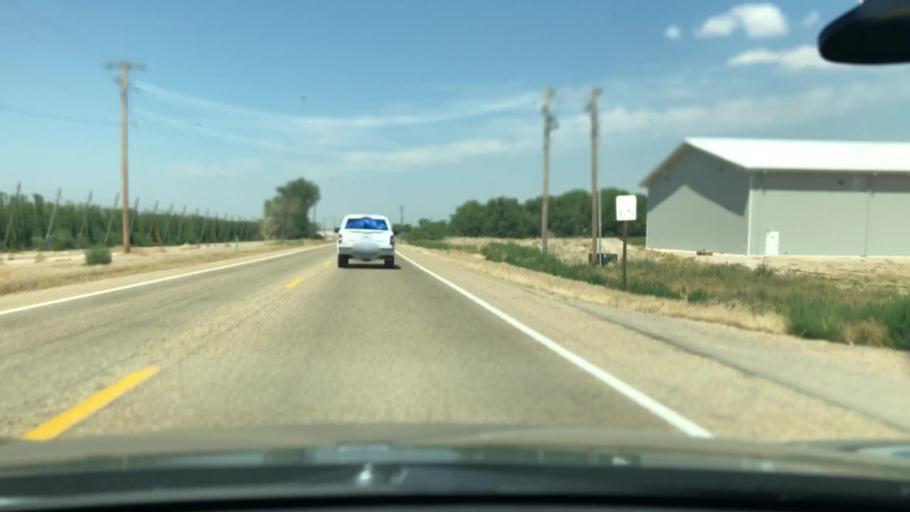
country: US
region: Idaho
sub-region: Canyon County
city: Wilder
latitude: 43.7062
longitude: -116.9119
